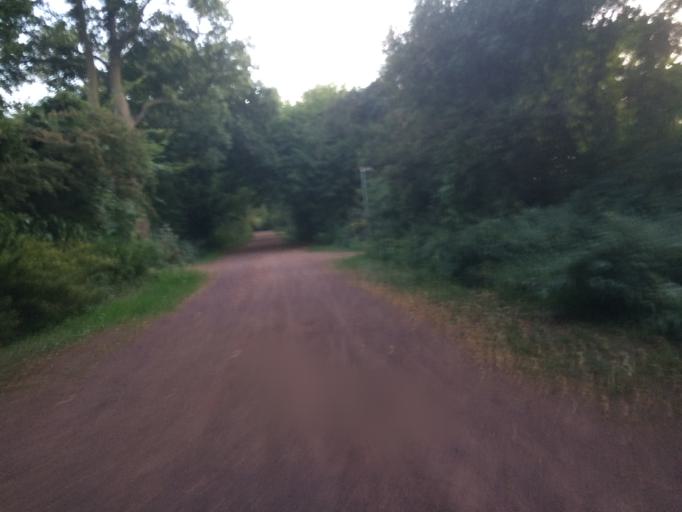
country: DE
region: Berlin
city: Stadtrandsiedlung Malchow
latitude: 52.5759
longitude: 13.4646
